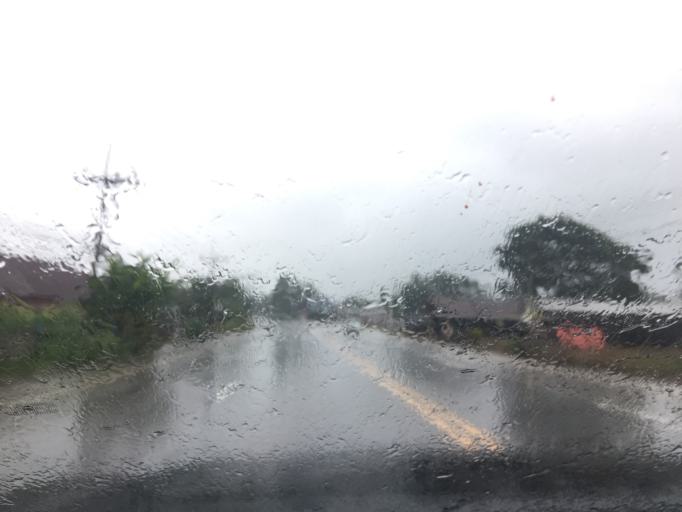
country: TH
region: Chiang Rai
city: Chiang Saen
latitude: 20.2879
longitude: 100.2195
